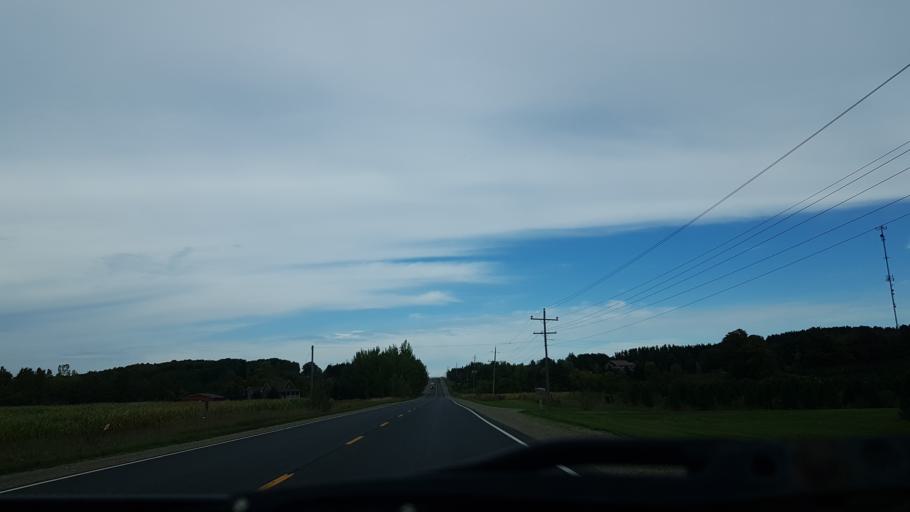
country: CA
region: Ontario
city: Angus
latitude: 44.3229
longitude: -80.0752
